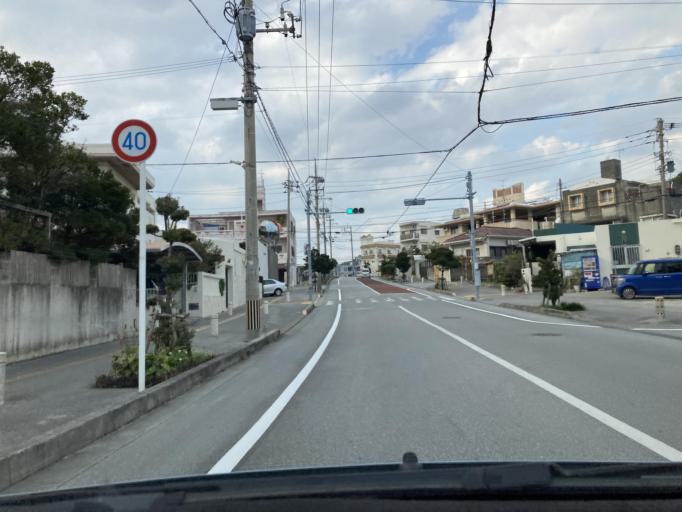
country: JP
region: Okinawa
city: Tomigusuku
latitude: 26.1956
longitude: 127.7333
